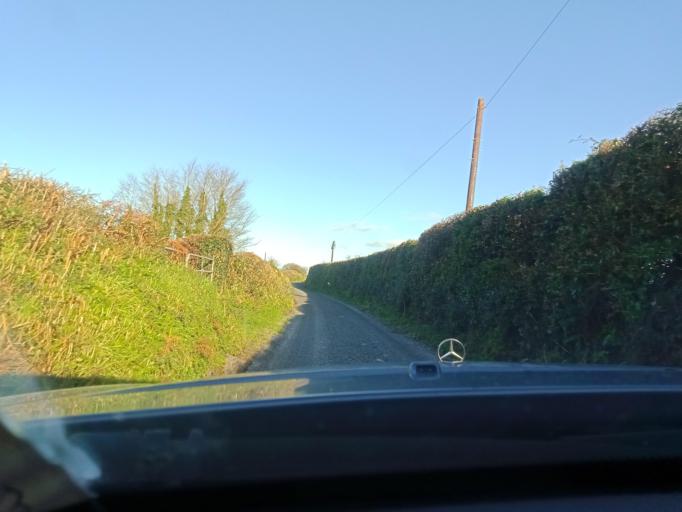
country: IE
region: Leinster
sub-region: Kilkenny
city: Graiguenamanagh
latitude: 52.5541
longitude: -6.9481
